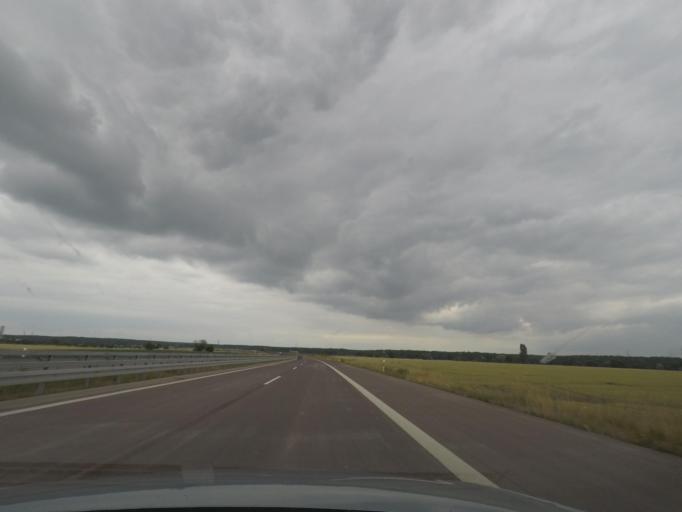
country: DE
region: Saxony-Anhalt
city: Colbitz
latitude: 52.3196
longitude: 11.6285
